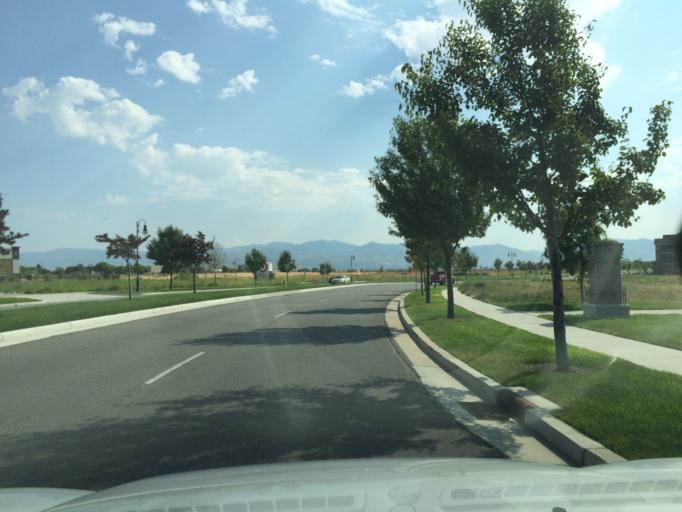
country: US
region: Utah
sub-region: Salt Lake County
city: West Valley City
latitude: 40.7119
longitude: -112.0211
